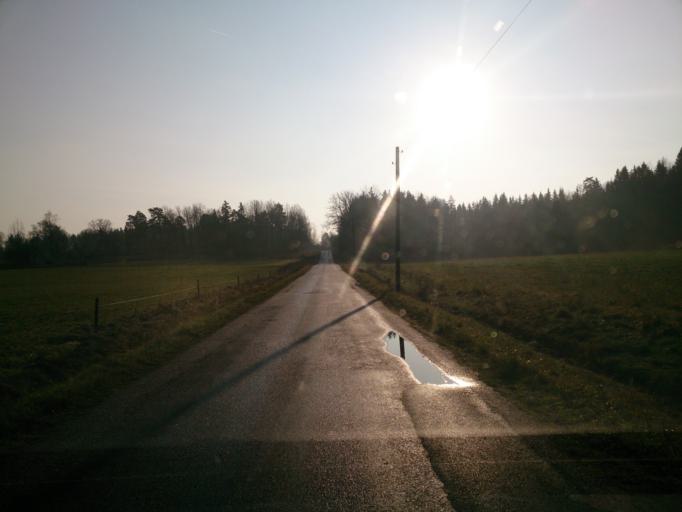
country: SE
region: OEstergoetland
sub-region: Atvidabergs Kommun
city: Atvidaberg
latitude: 58.3308
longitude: 16.0234
